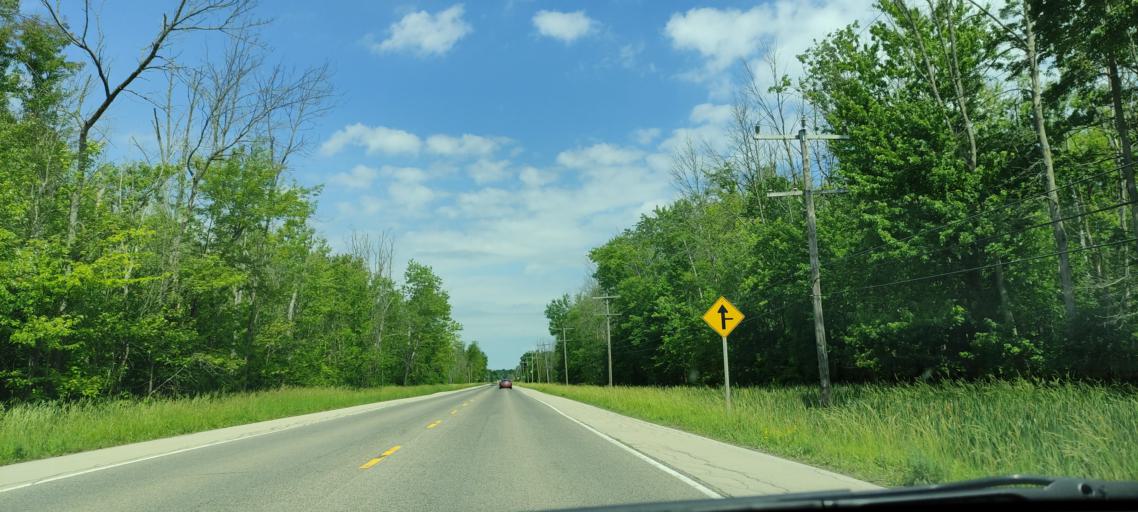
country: CA
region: Ontario
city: Burlington
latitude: 43.3634
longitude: -79.9395
